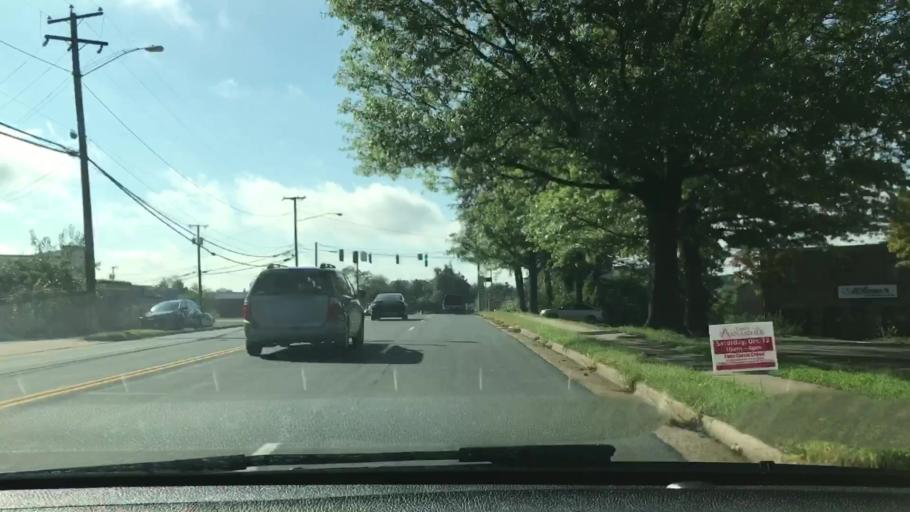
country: US
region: Virginia
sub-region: Fairfax County
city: Annandale
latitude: 38.8332
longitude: -77.1972
